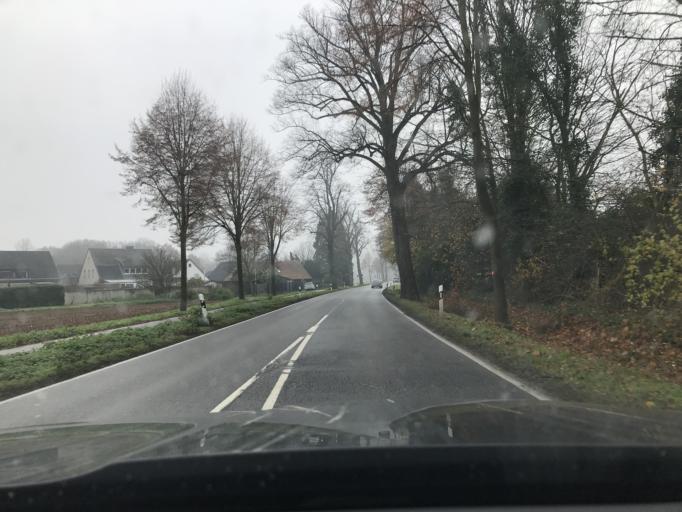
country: DE
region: North Rhine-Westphalia
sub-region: Regierungsbezirk Dusseldorf
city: Nettetal
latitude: 51.2871
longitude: 6.2624
